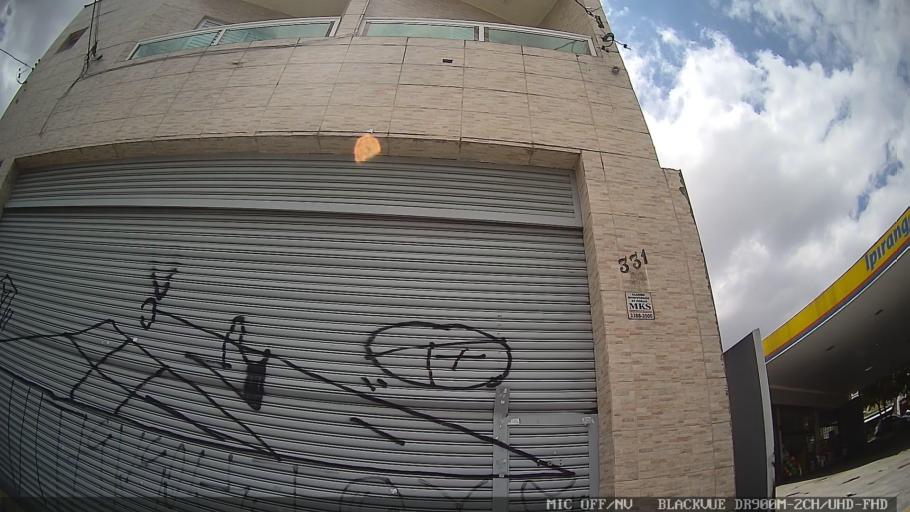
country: BR
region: Sao Paulo
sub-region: Guarulhos
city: Guarulhos
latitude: -23.5366
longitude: -46.4954
